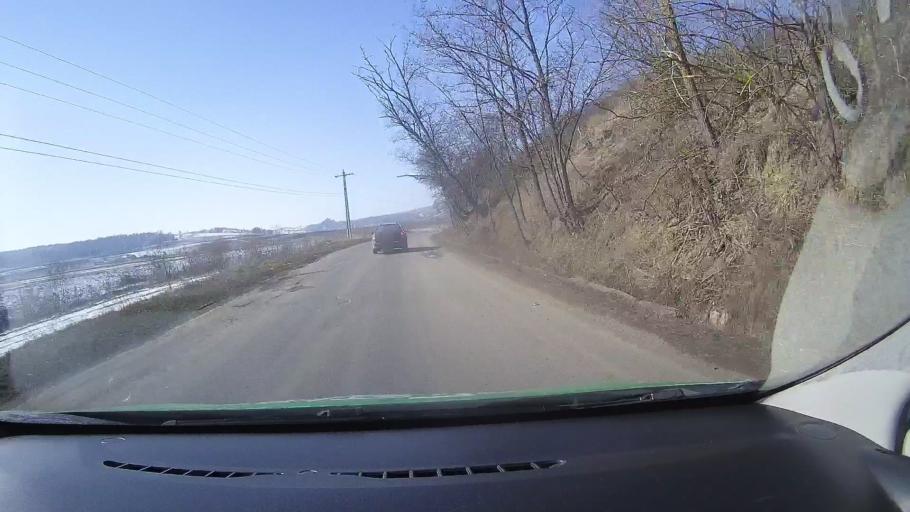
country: RO
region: Brasov
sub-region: Comuna Homorod
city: Homorod
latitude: 46.0375
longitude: 25.2659
